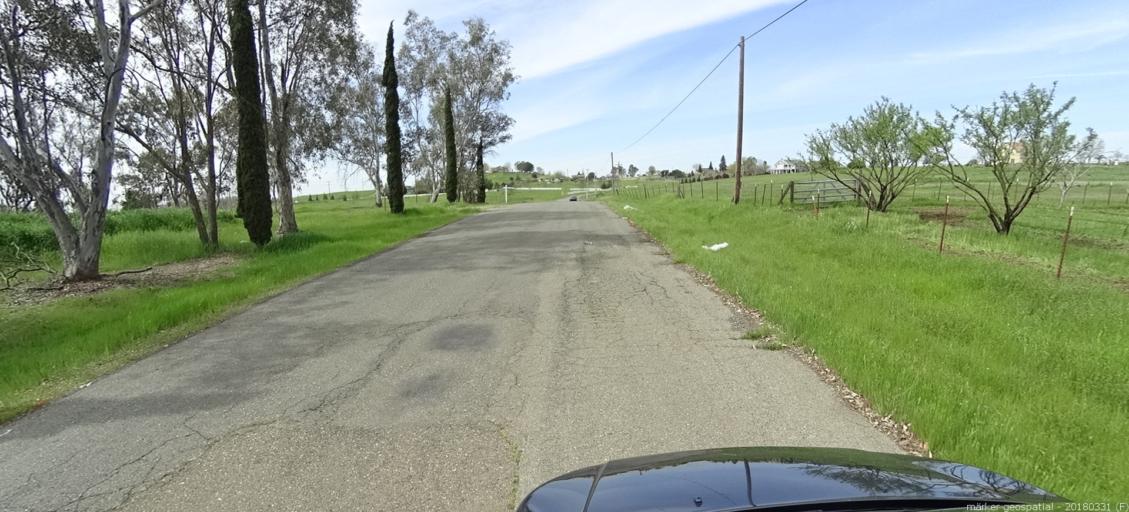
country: US
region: California
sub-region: Sacramento County
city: Rancho Murieta
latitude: 38.4982
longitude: -121.1177
